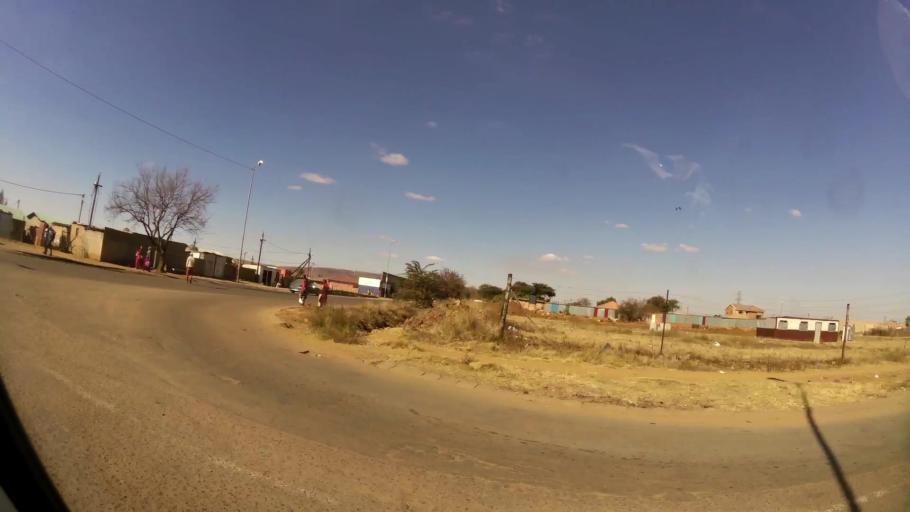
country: ZA
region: Gauteng
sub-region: City of Tshwane Metropolitan Municipality
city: Cullinan
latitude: -25.7103
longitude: 28.3984
